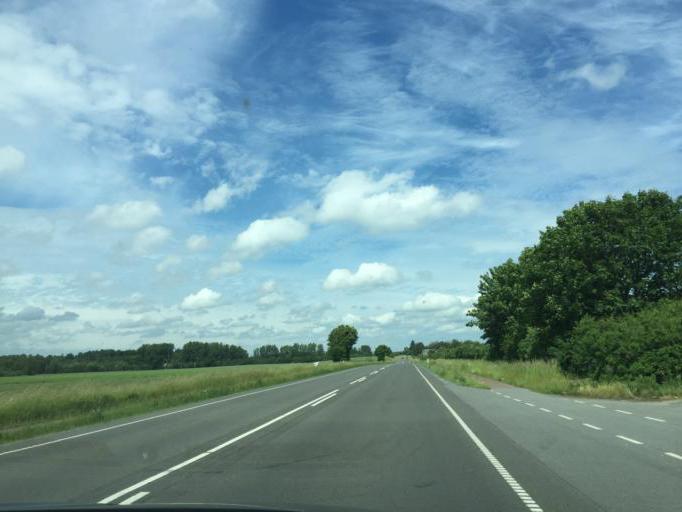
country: DK
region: South Denmark
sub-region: Odense Kommune
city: Hojby
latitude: 55.3104
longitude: 10.3993
